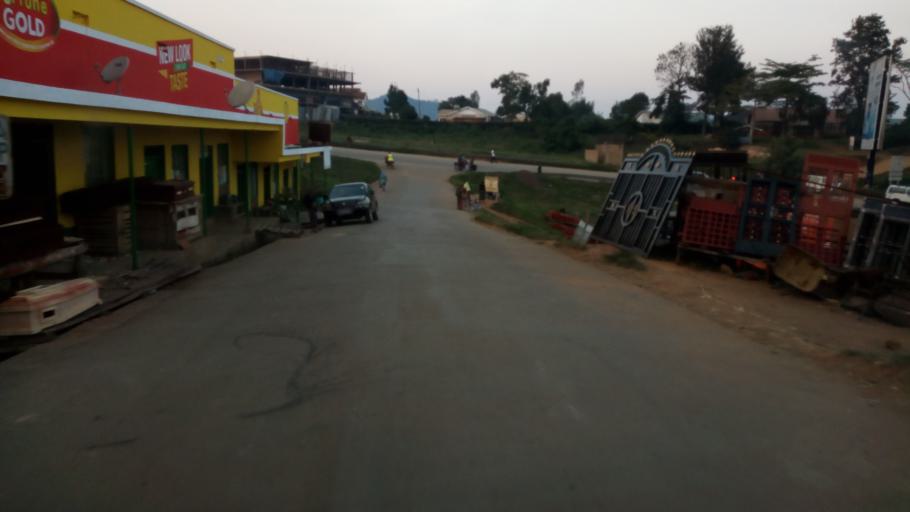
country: UG
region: Western Region
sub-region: Rukungiri District
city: Rukungiri
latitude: -0.7916
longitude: 29.9269
